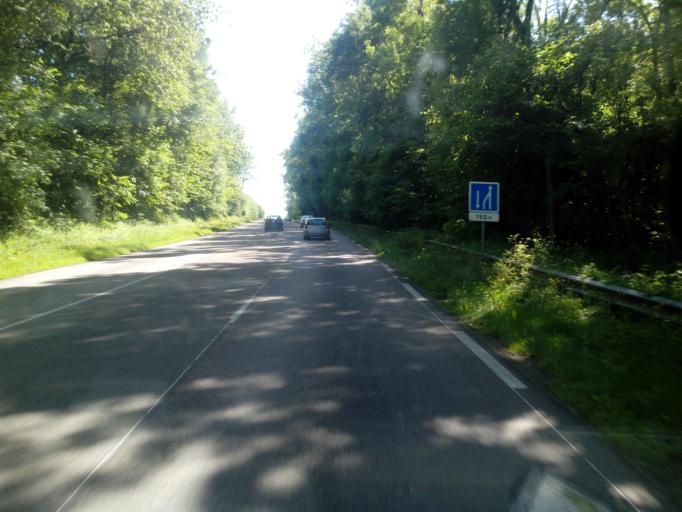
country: FR
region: Haute-Normandie
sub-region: Departement de l'Eure
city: Toutainville
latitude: 49.3814
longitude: 0.4008
